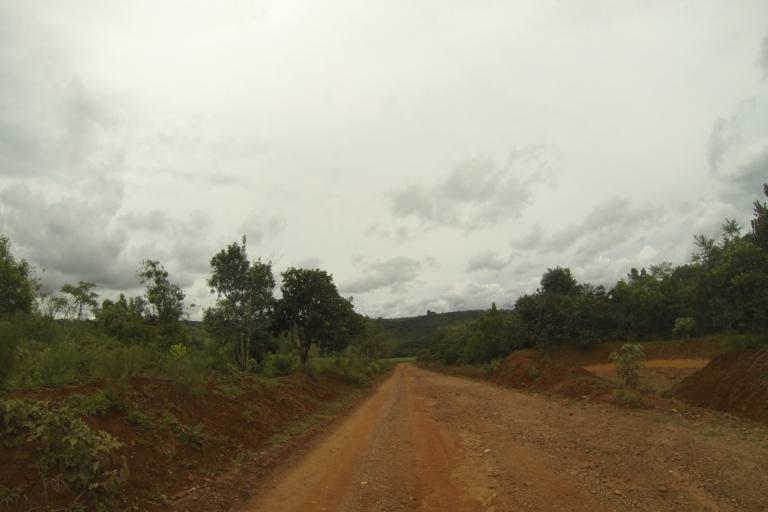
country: BR
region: Minas Gerais
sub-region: Ibia
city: Ibia
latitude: -19.6603
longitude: -46.7013
